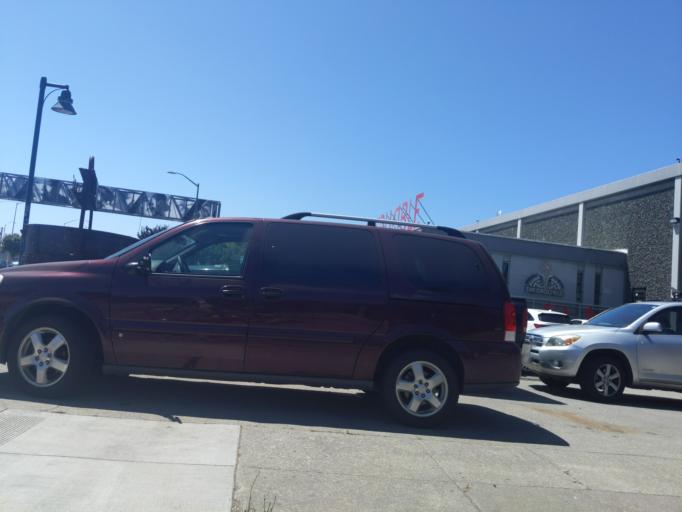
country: US
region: California
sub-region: Alameda County
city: Oakland
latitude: 37.8045
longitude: -122.2904
